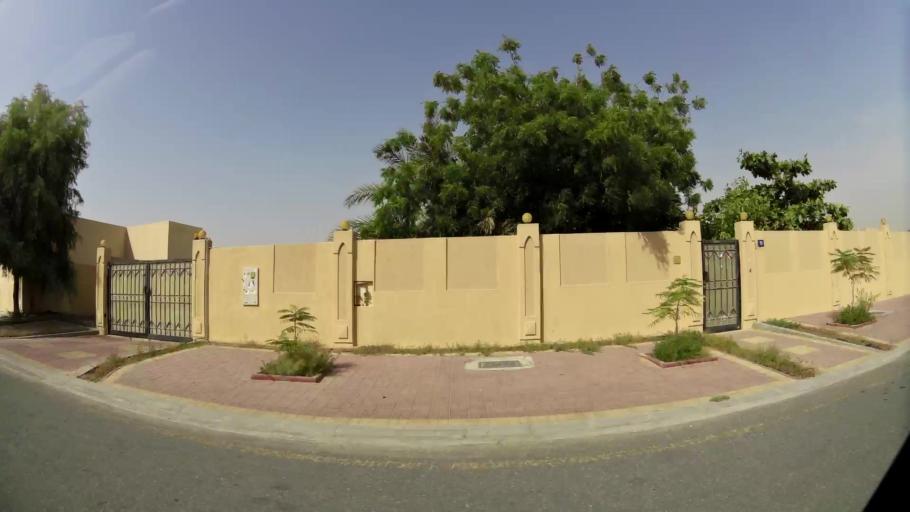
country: AE
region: Ash Shariqah
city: Sharjah
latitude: 25.2579
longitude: 55.4319
